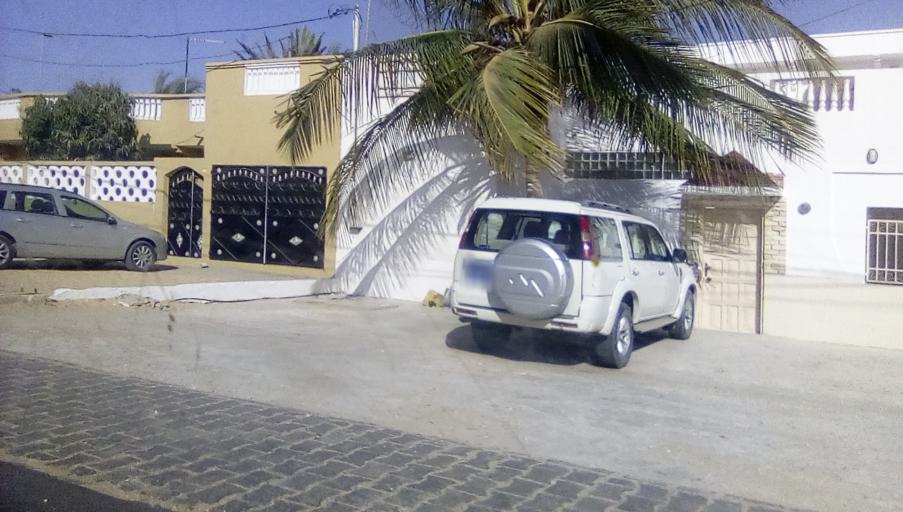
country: SN
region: Saint-Louis
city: Saint-Louis
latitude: 16.0324
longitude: -16.4714
